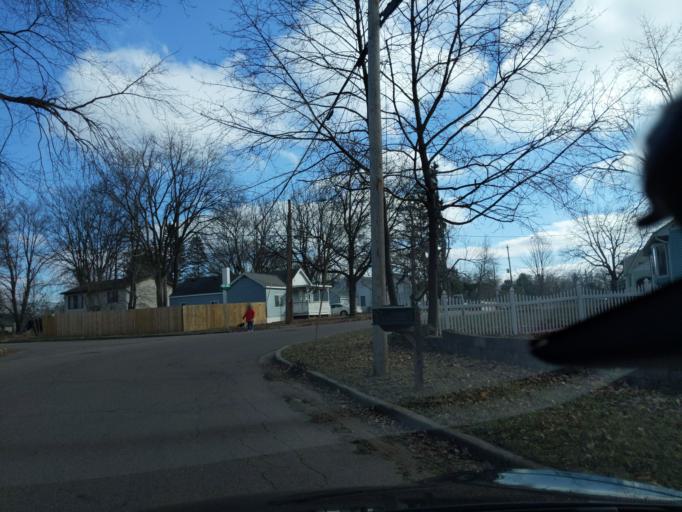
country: US
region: Michigan
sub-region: Ingham County
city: Lansing
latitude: 42.6730
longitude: -84.5813
